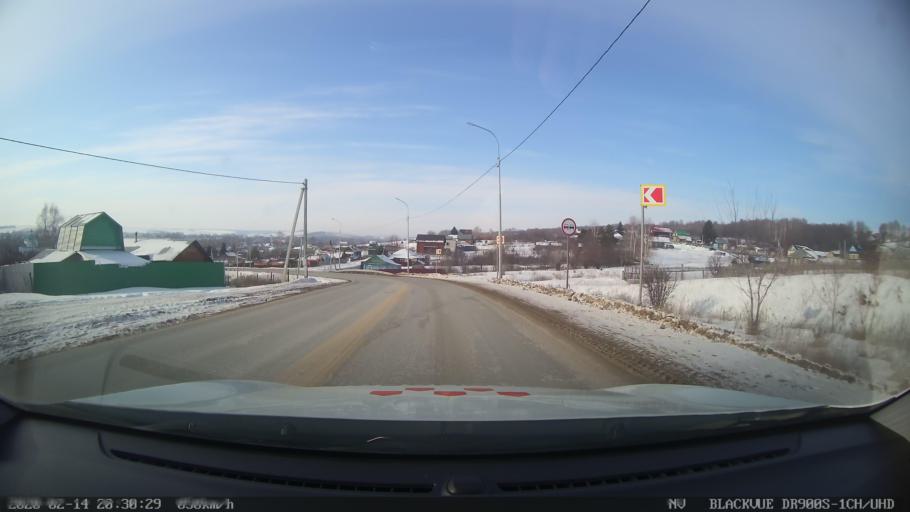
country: RU
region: Tatarstan
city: Stolbishchi
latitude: 55.4427
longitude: 48.9928
